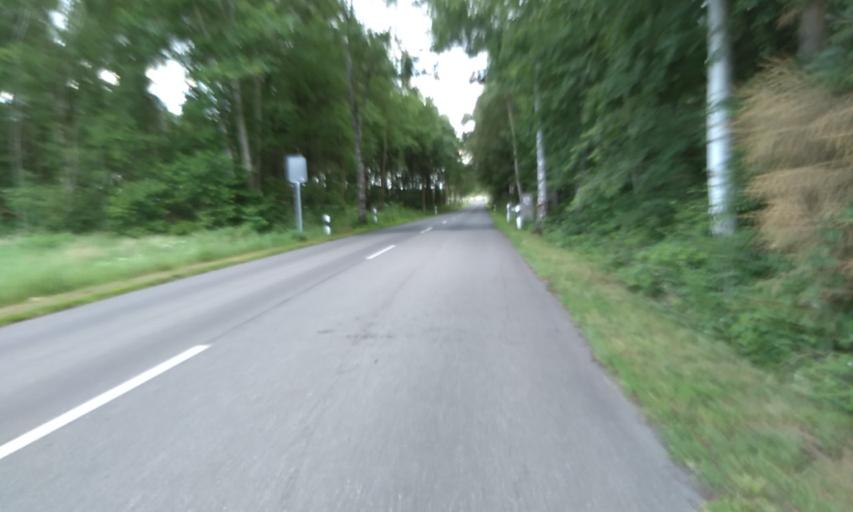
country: DE
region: Lower Saxony
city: Halvesbostel
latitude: 53.3571
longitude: 9.5712
